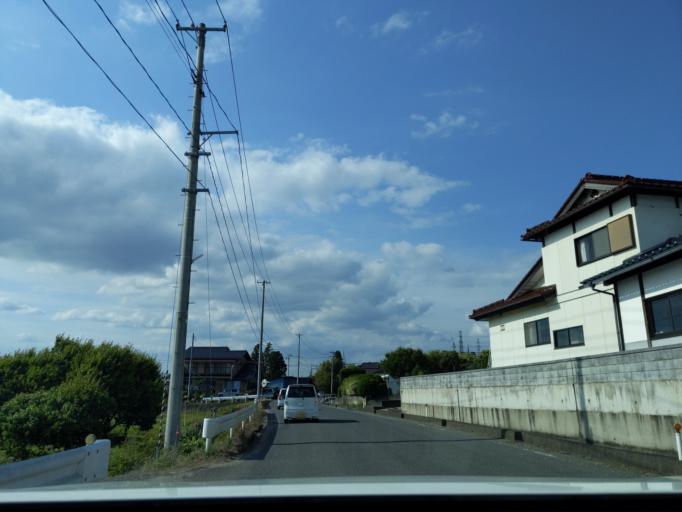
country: JP
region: Fukushima
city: Koriyama
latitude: 37.3746
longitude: 140.4110
